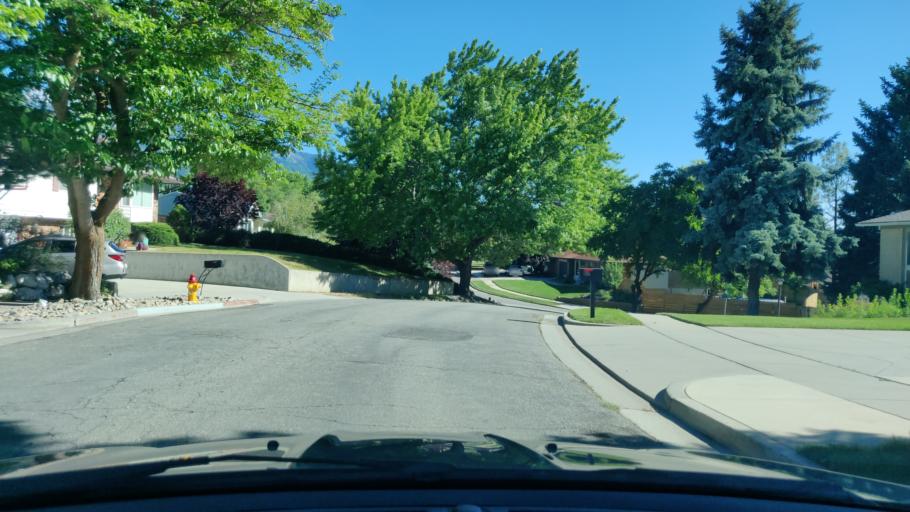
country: US
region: Utah
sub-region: Salt Lake County
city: Cottonwood Heights
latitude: 40.6131
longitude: -111.8060
